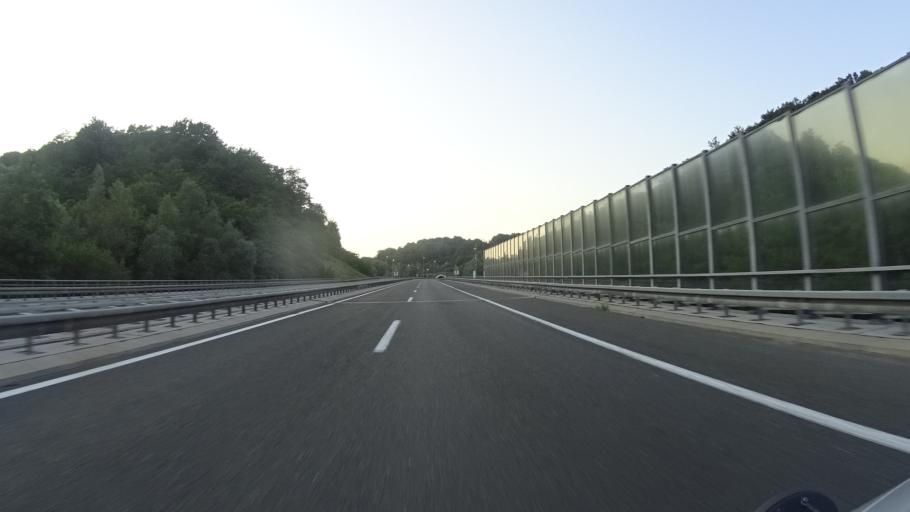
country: HR
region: Varazdinska
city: Ljubescica
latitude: 46.1971
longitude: 16.4119
